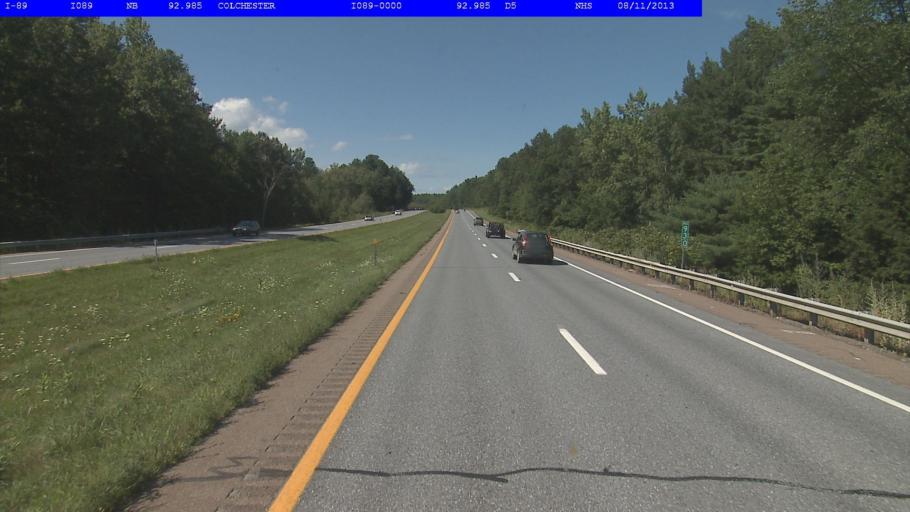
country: US
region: Vermont
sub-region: Chittenden County
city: Winooski
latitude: 44.5239
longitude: -73.1931
